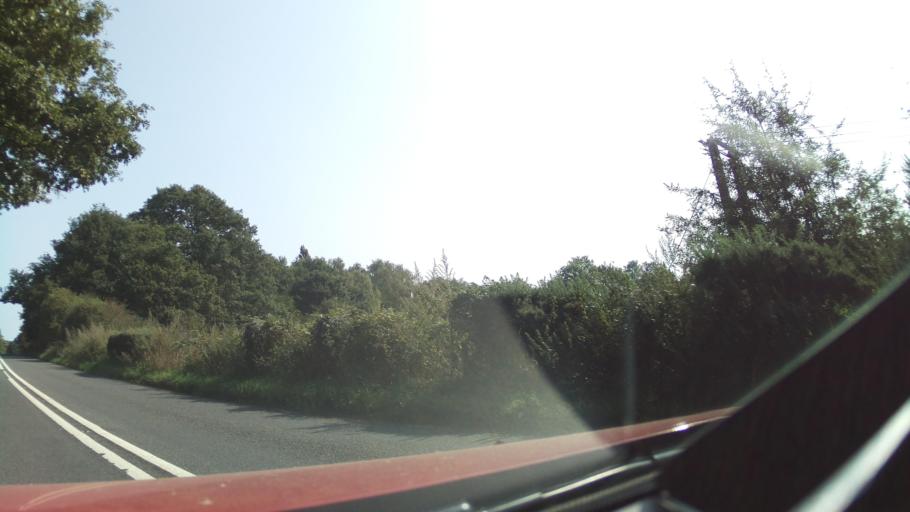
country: GB
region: England
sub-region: Staffordshire
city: Lichfield
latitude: 52.6667
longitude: -1.8700
